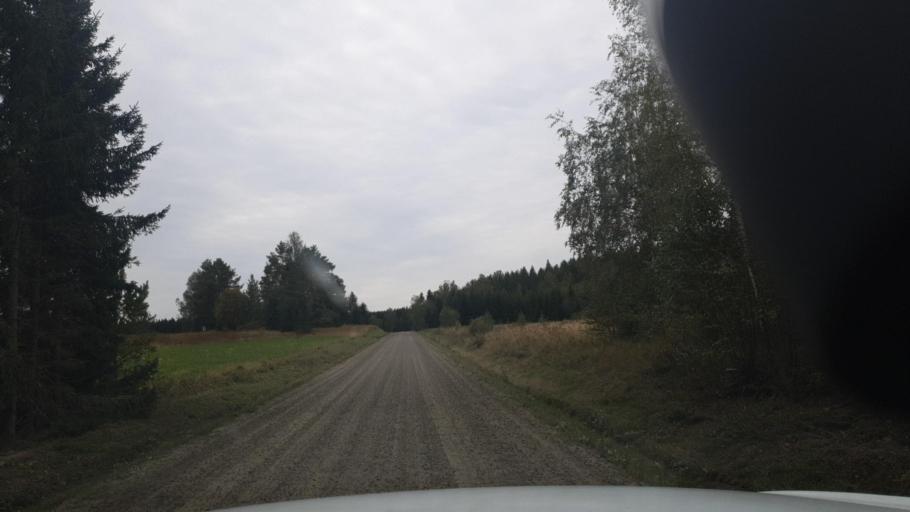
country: SE
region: Vaermland
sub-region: Karlstads Kommun
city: Edsvalla
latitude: 59.5503
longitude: 13.0101
